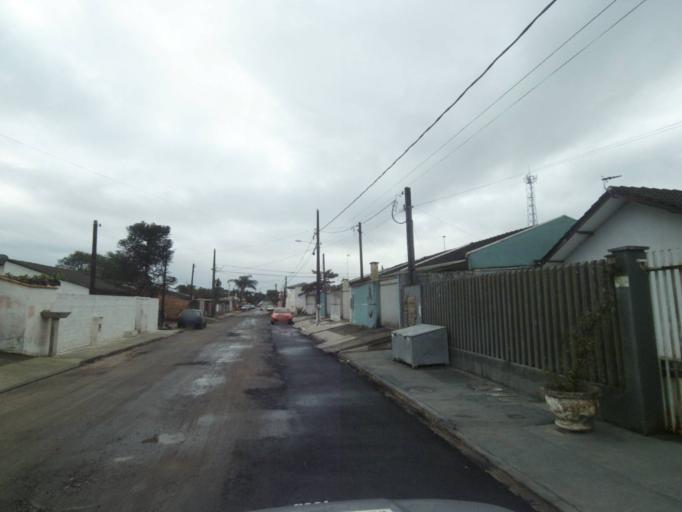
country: BR
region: Parana
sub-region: Paranagua
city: Paranagua
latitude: -25.5636
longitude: -48.5708
